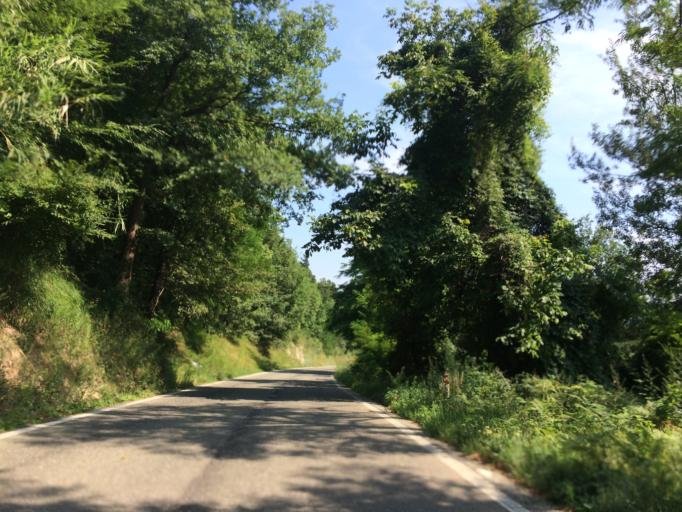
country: IT
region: Piedmont
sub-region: Provincia di Cuneo
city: Cravanzana
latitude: 44.5750
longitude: 8.1431
